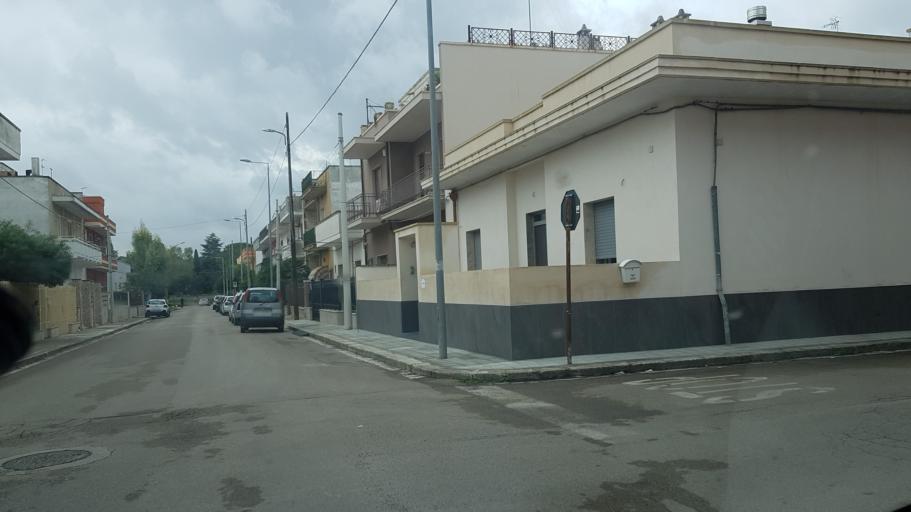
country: IT
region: Apulia
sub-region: Provincia di Lecce
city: Novoli
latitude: 40.3733
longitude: 18.0466
